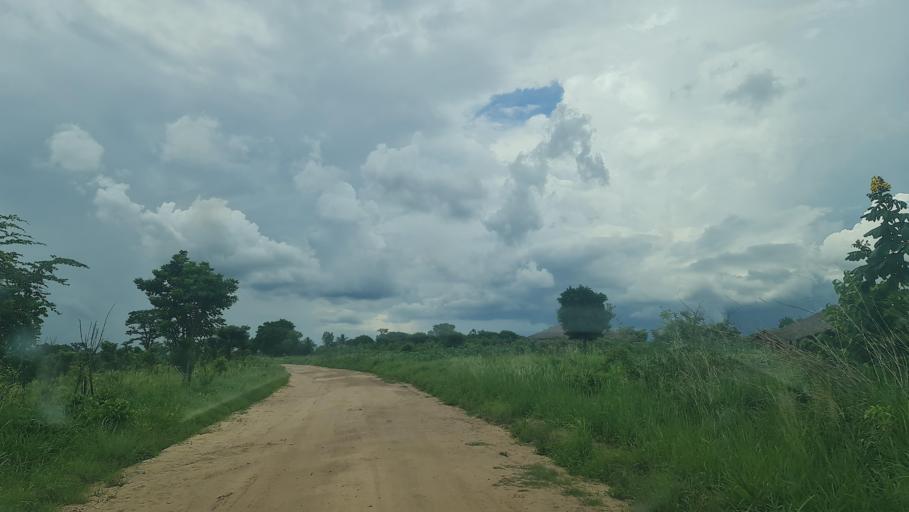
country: MW
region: Southern Region
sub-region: Nsanje District
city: Nsanje
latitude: -17.5779
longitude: 35.6600
